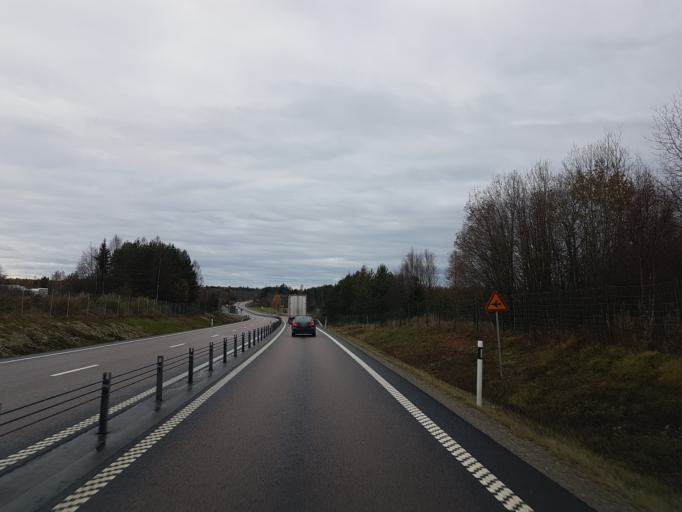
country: SE
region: Gaevleborg
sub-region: Hudiksvalls Kommun
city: Hudiksvall
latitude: 61.7671
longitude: 17.0966
